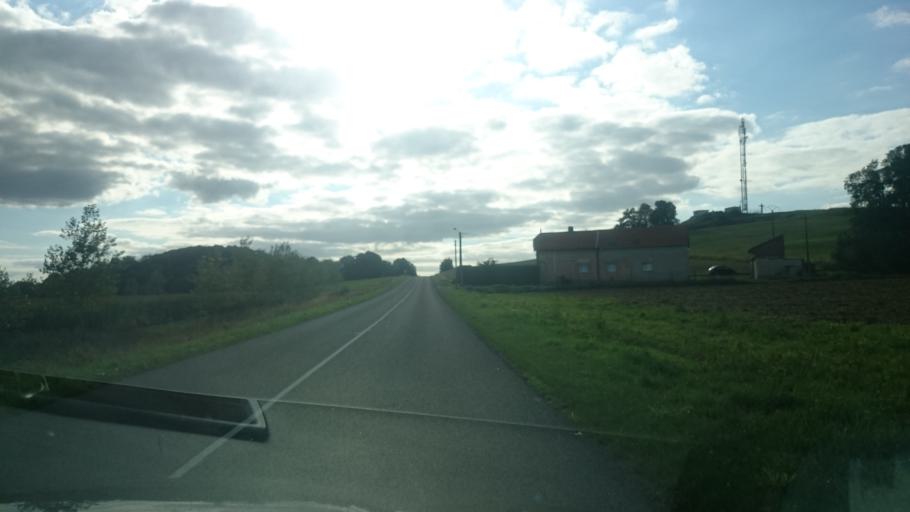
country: FR
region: Picardie
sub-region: Departement de l'Aisne
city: Sinceny
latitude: 49.6036
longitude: 3.2926
